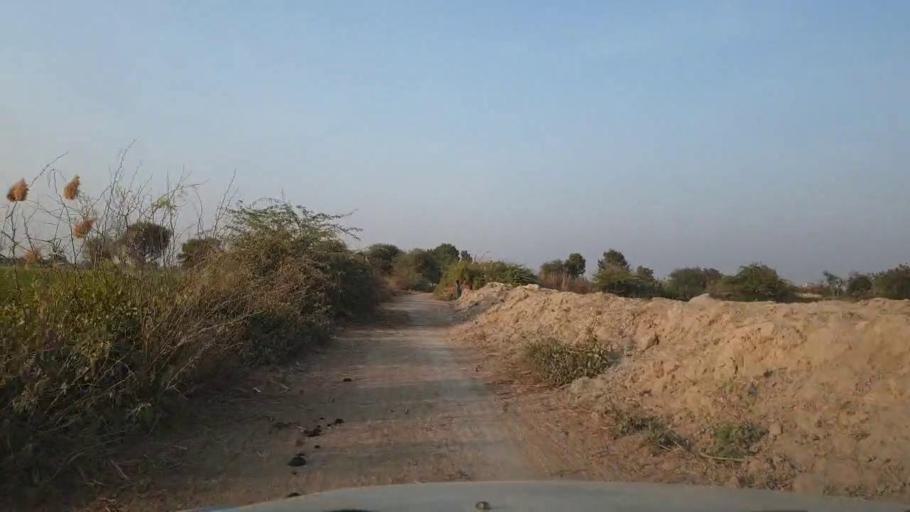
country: PK
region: Sindh
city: Pithoro
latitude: 25.6545
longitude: 69.2127
